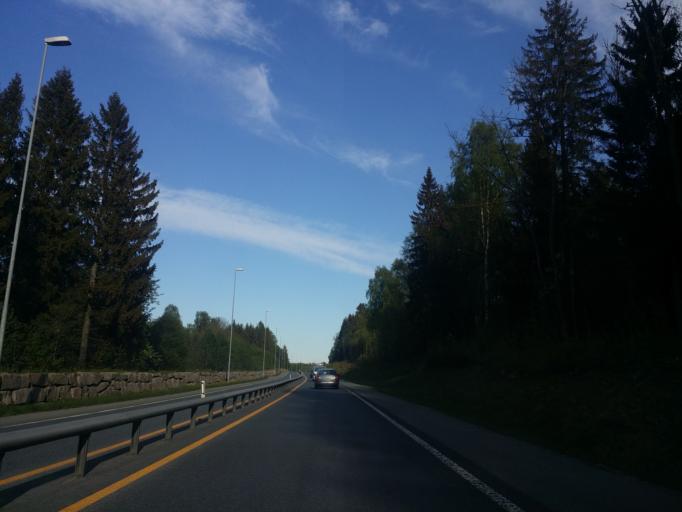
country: NO
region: Buskerud
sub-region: Drammen
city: Drammen
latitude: 59.7431
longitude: 10.1238
